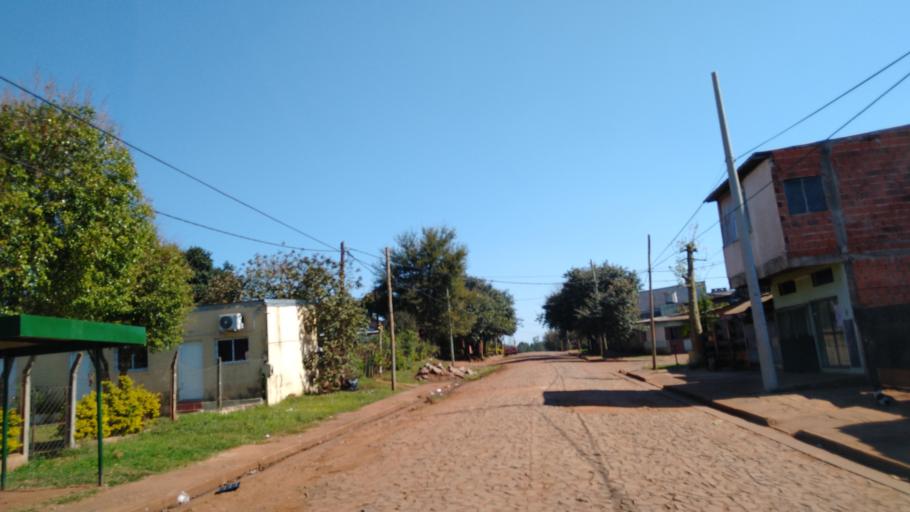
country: AR
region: Misiones
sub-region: Departamento de Capital
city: Posadas
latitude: -27.4188
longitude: -55.9598
